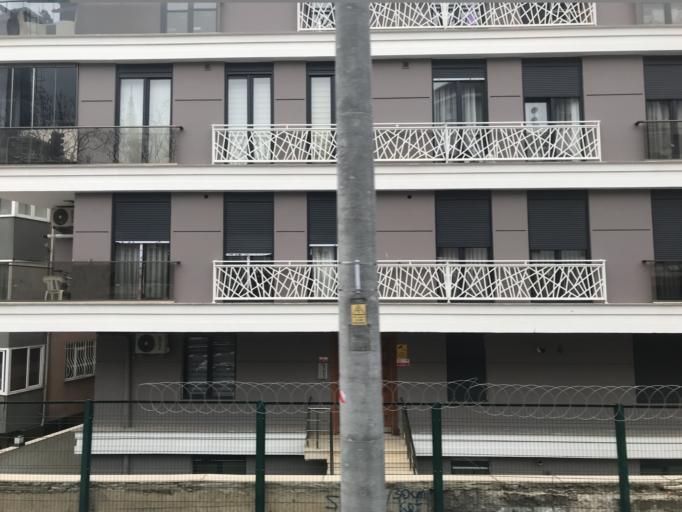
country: TR
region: Istanbul
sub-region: Atasehir
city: Atasehir
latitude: 40.9463
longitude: 29.1084
